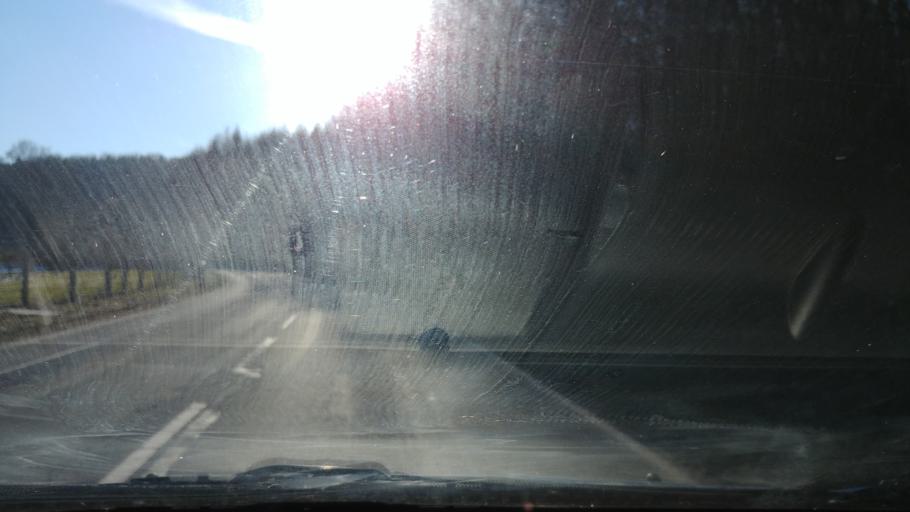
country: DE
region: Hesse
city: Trendelburg
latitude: 51.5729
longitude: 9.4812
